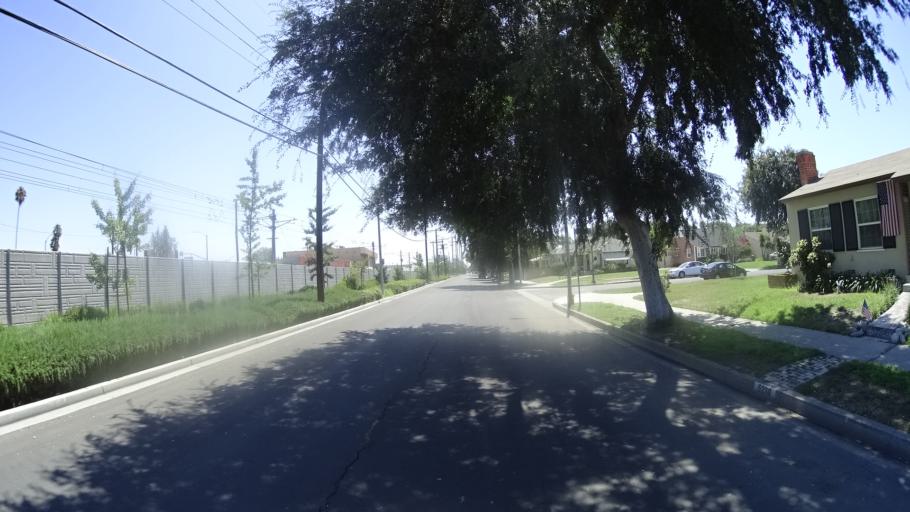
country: US
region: California
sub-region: Los Angeles County
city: View Park-Windsor Hills
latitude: 34.0251
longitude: -118.3597
